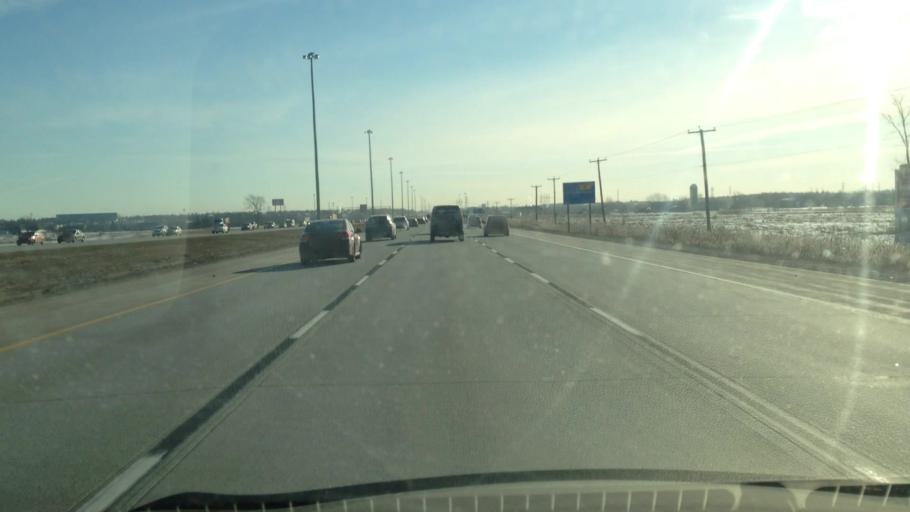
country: CA
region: Quebec
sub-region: Laurentides
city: Blainville
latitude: 45.7001
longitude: -73.9489
